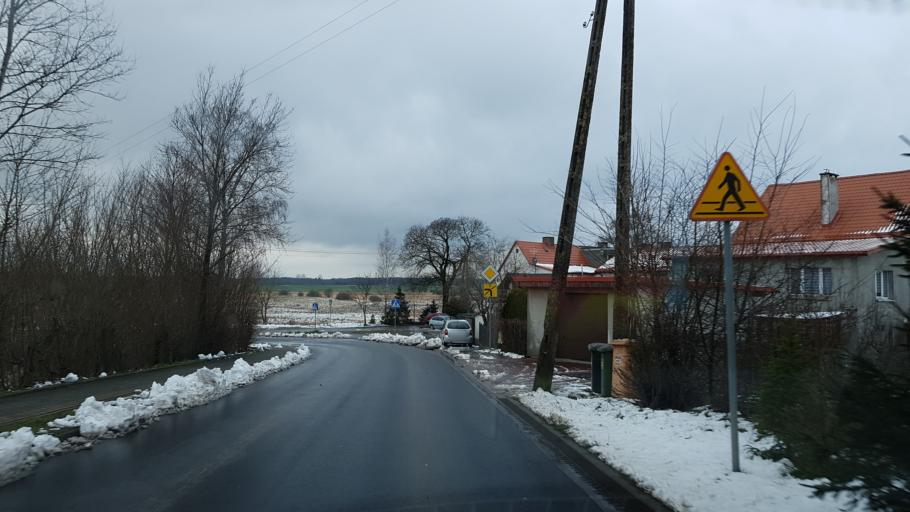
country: PL
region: West Pomeranian Voivodeship
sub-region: Powiat slawienski
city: Slawno
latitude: 54.3711
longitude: 16.6764
